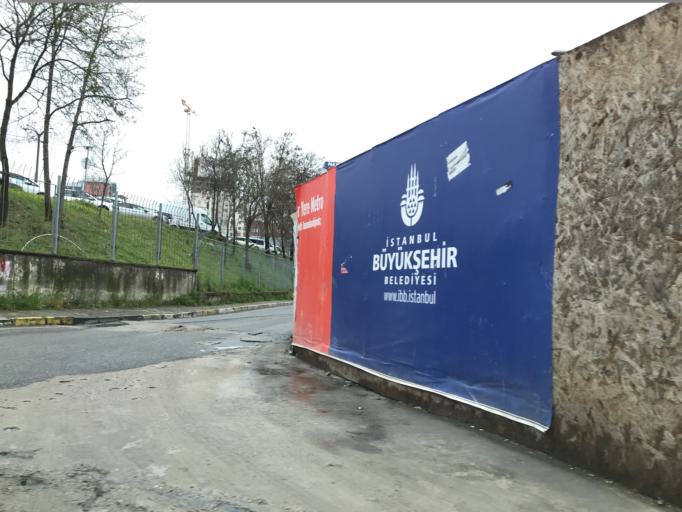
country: TR
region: Istanbul
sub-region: Atasehir
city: Atasehir
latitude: 40.9853
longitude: 29.0931
